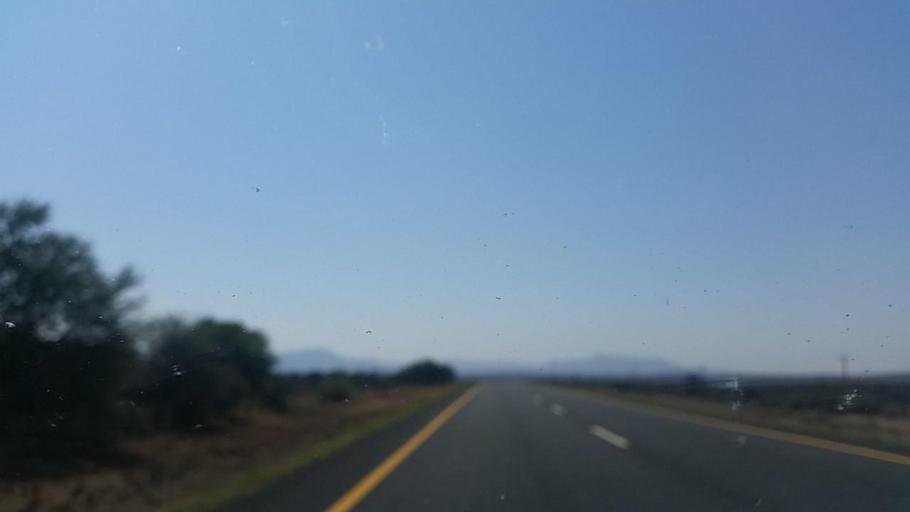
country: ZA
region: Eastern Cape
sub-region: Cacadu District Municipality
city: Graaff-Reinet
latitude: -32.3425
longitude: 24.4034
